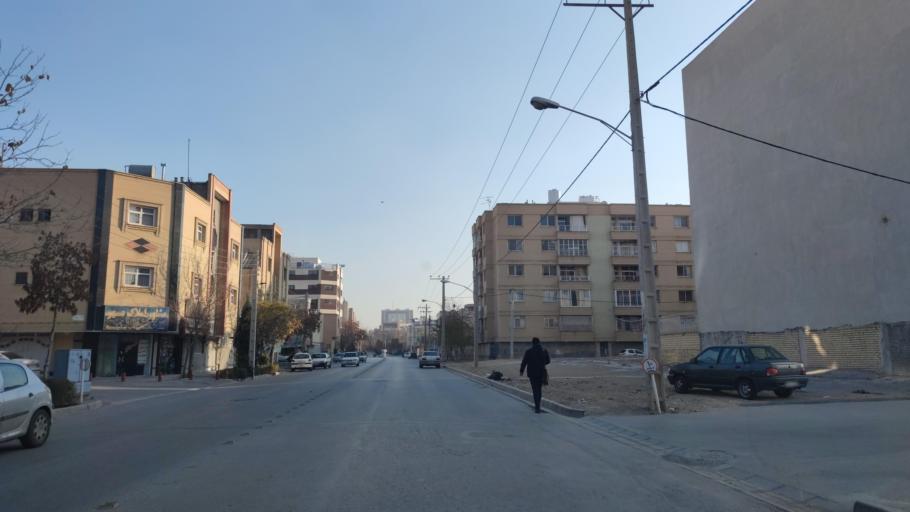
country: IR
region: Isfahan
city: Isfahan
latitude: 32.7114
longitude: 51.6850
